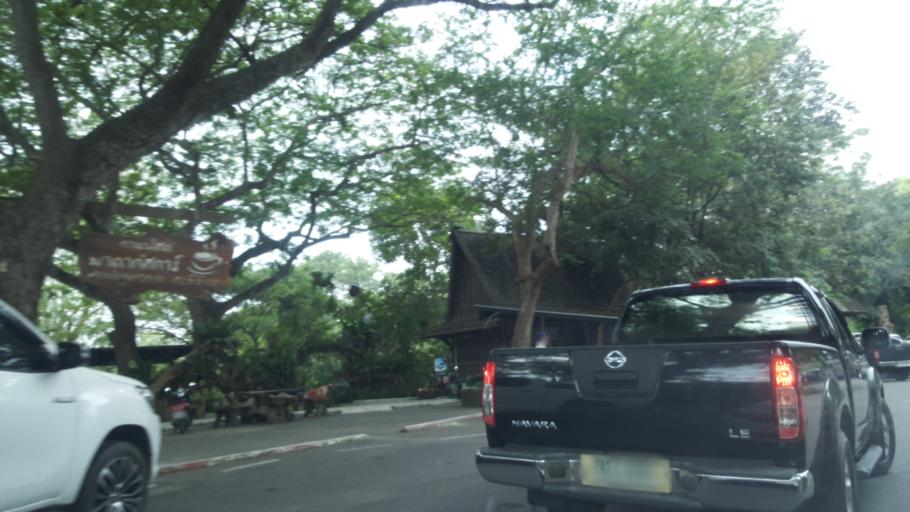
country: TH
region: Chon Buri
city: Ban Bueng
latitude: 13.2171
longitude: 101.0543
